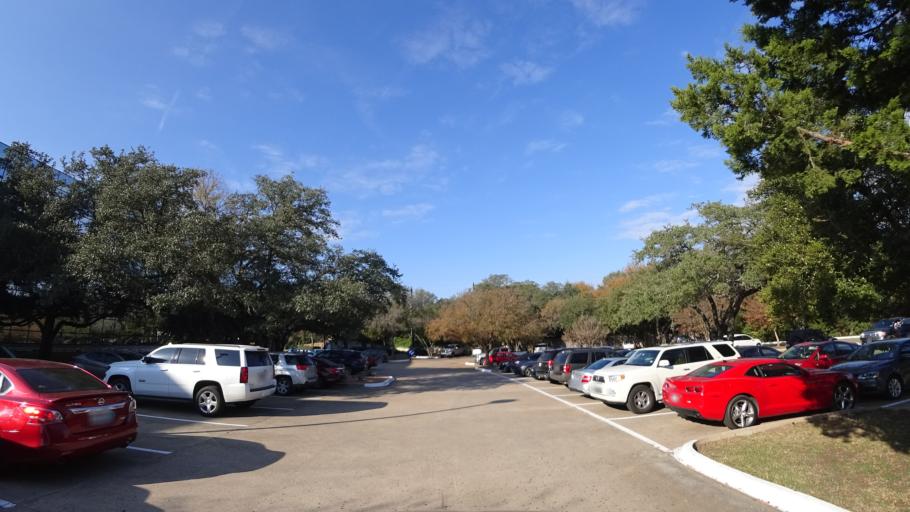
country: US
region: Texas
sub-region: Williamson County
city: Jollyville
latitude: 30.3959
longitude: -97.7538
